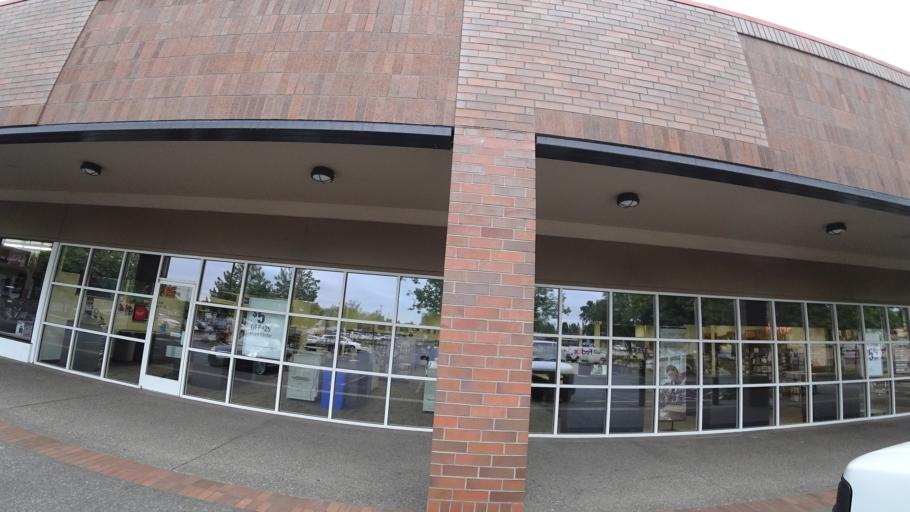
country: US
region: Oregon
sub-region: Washington County
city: Beaverton
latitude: 45.4872
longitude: -122.7978
